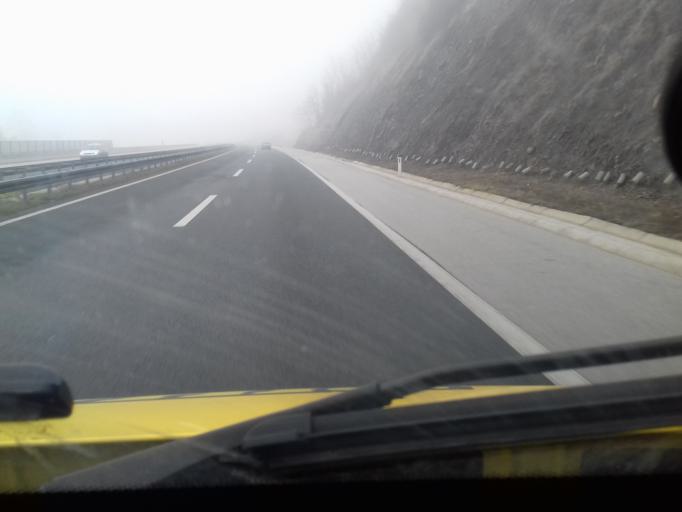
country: BA
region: Federation of Bosnia and Herzegovina
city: Dobrinje
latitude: 44.0601
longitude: 18.1024
